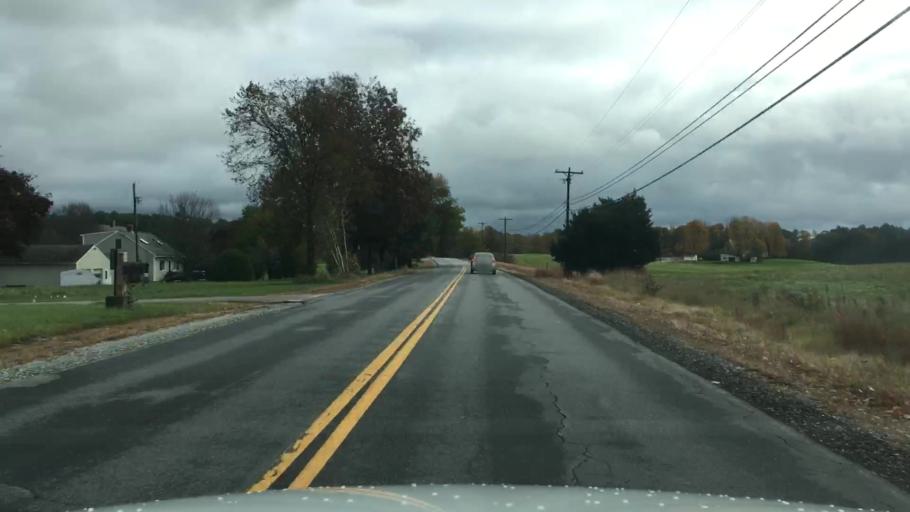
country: US
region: New Hampshire
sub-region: Strafford County
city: Lee
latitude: 43.1063
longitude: -70.9941
